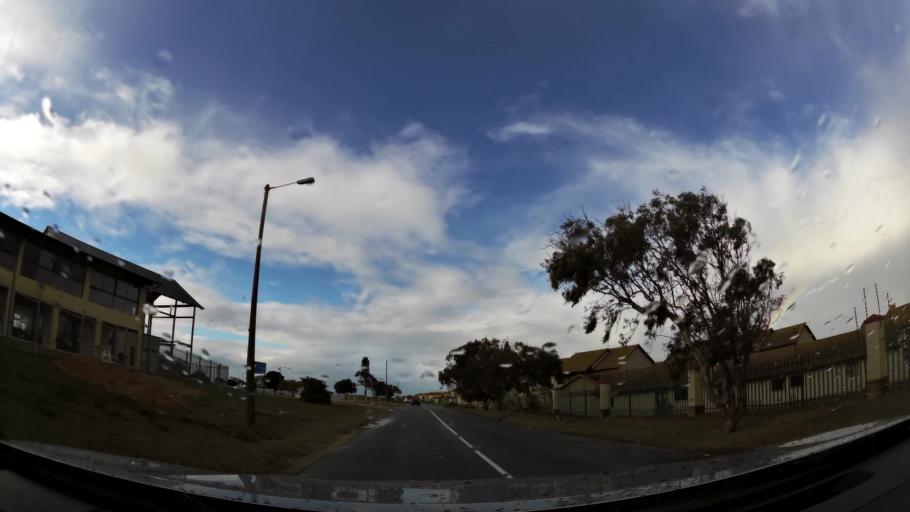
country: ZA
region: Western Cape
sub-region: Eden District Municipality
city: Mossel Bay
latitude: -34.1902
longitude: 22.1220
